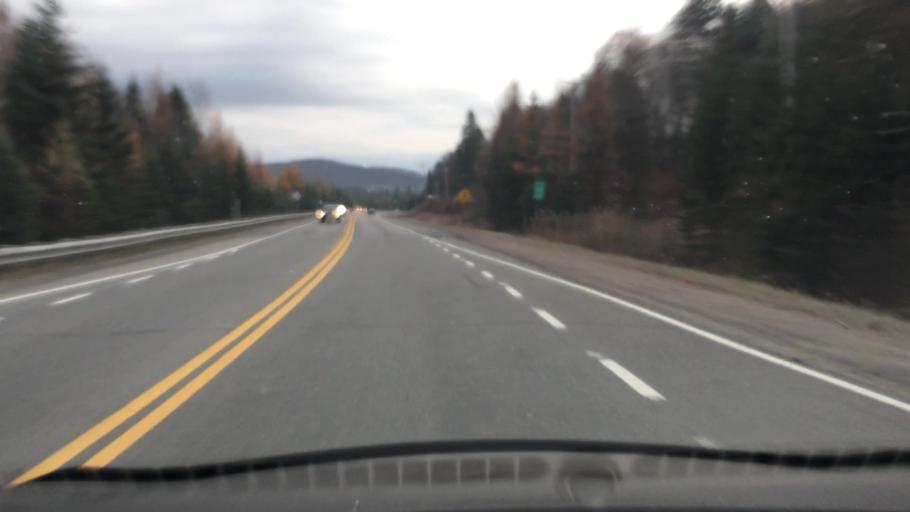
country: CA
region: Quebec
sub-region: Laurentides
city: Saint-Sauveur
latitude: 45.9001
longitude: -74.2220
